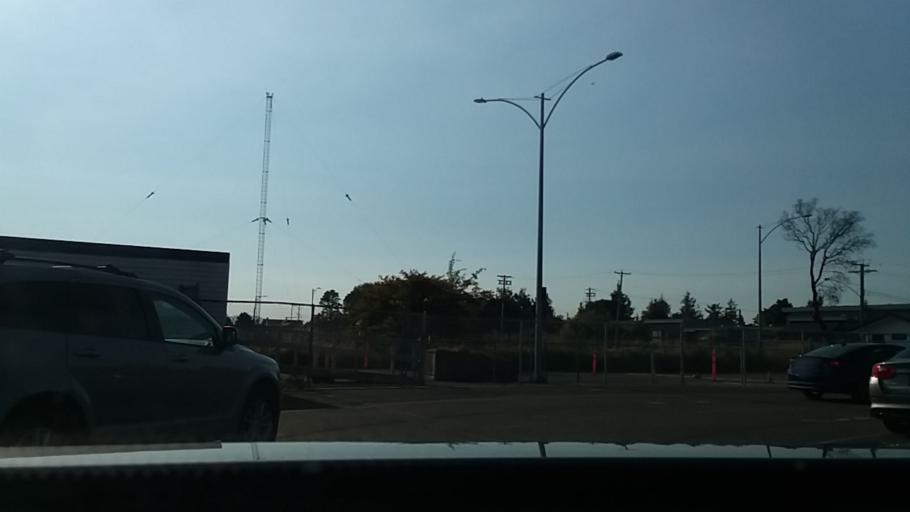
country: CA
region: British Columbia
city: North Saanich
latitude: 48.6439
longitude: -123.3985
